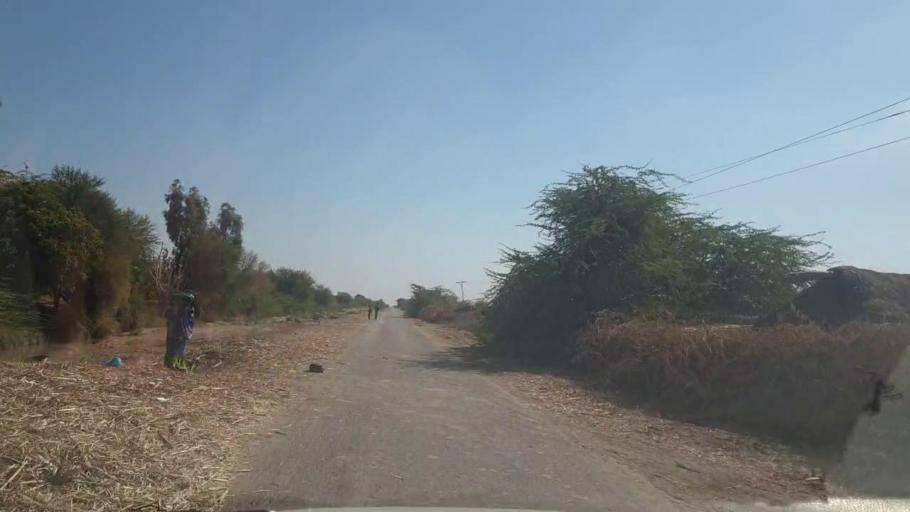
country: PK
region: Sindh
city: Mirpur Khas
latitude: 25.4793
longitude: 69.1726
